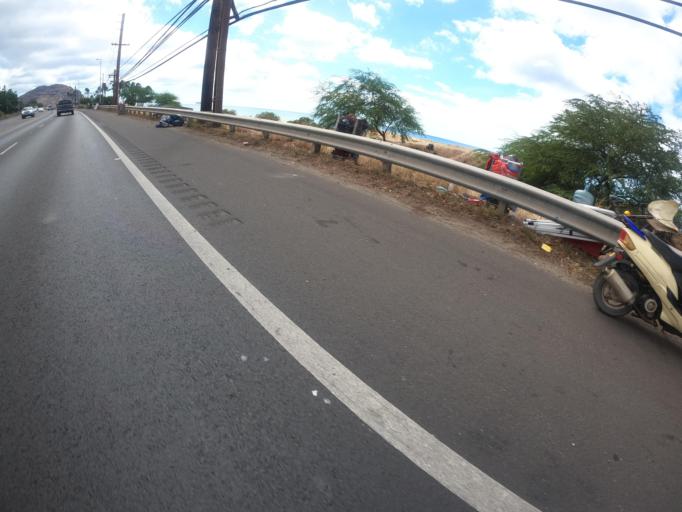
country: US
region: Hawaii
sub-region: Honolulu County
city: Waianae
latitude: 21.4342
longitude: -158.1845
